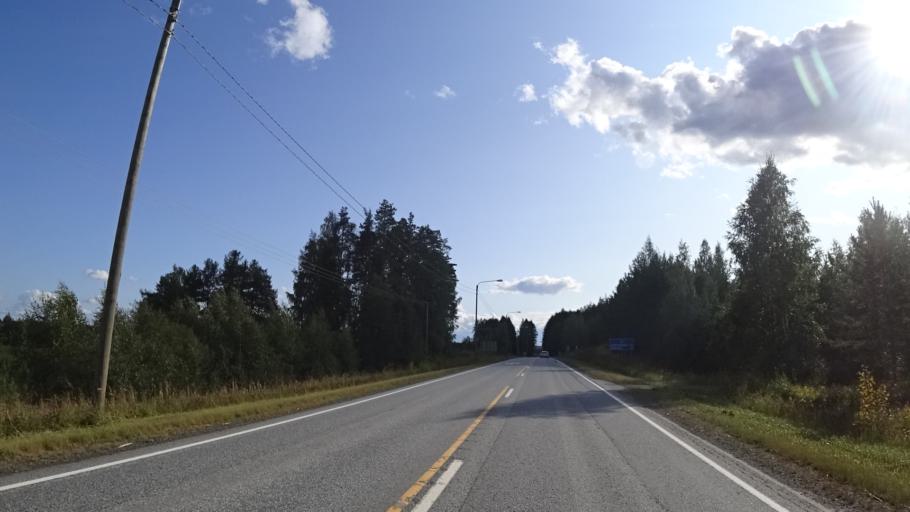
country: FI
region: North Karelia
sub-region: Keski-Karjala
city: Kitee
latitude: 62.0901
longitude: 29.9566
